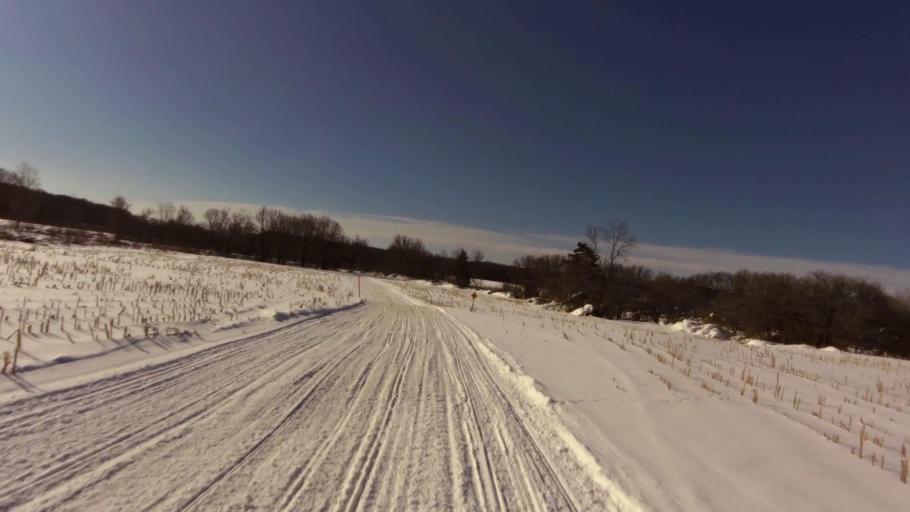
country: US
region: New York
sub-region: Cattaraugus County
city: Franklinville
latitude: 42.3972
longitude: -78.4732
